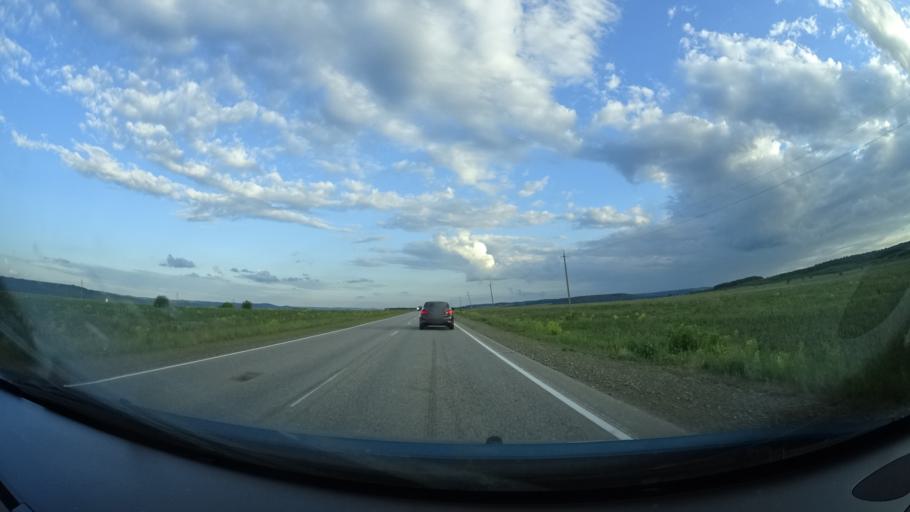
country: RU
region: Perm
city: Barda
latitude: 57.0449
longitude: 55.5456
